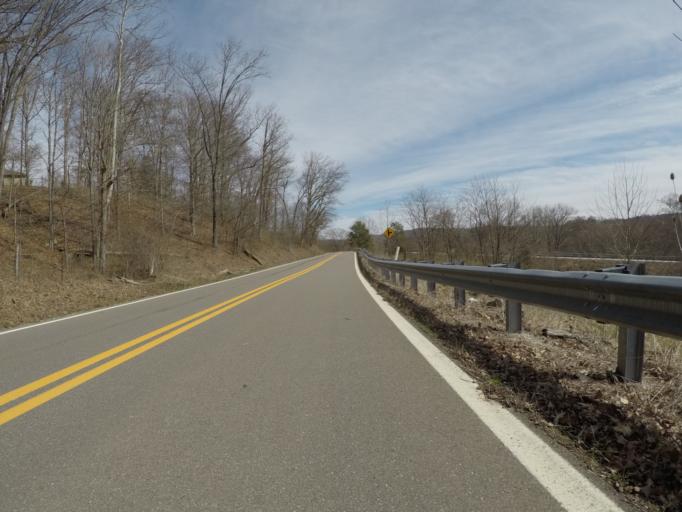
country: US
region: West Virginia
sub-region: Wayne County
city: Ceredo
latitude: 38.3735
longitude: -82.5396
